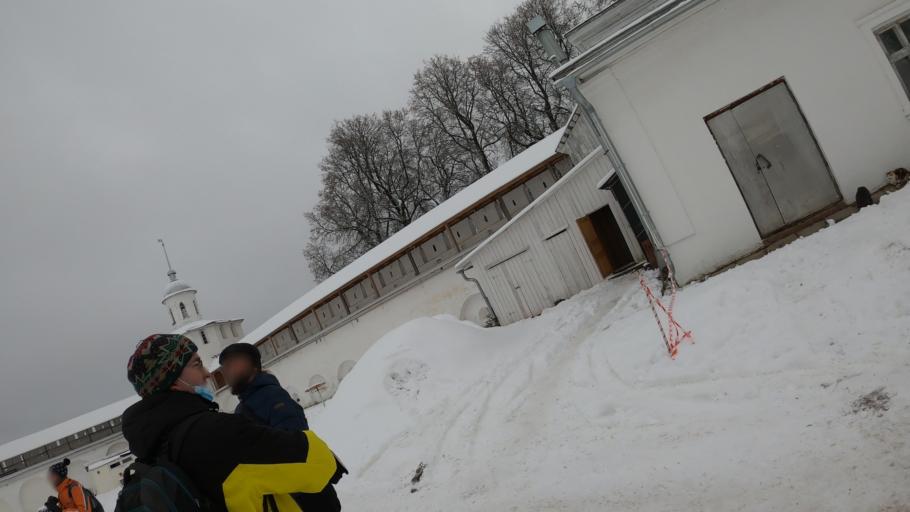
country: RU
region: Jaroslavl
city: Pereslavl'-Zalesskiy
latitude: 56.7614
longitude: 38.8596
